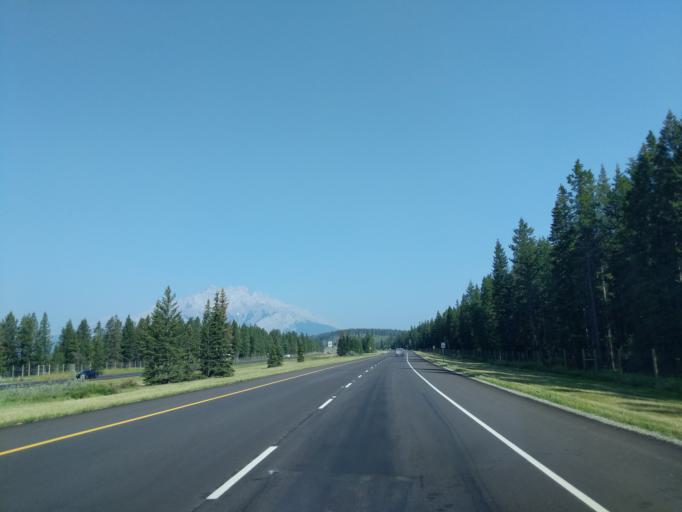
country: CA
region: Alberta
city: Canmore
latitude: 51.1527
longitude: -115.4318
